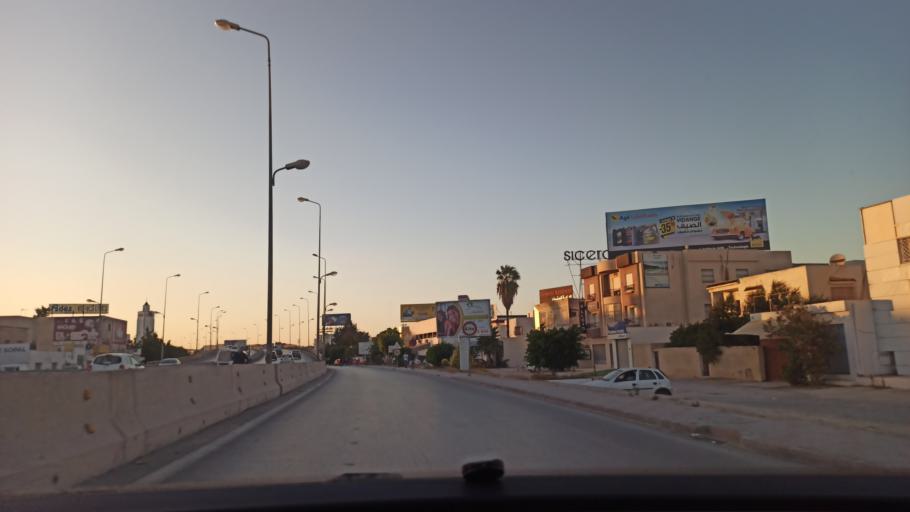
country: TN
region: Ariana
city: Ariana
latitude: 36.8624
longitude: 10.2020
